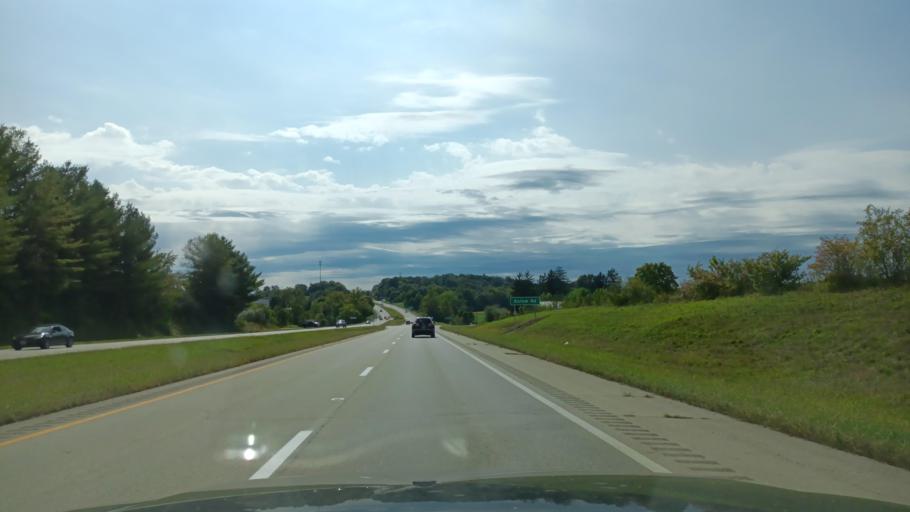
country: US
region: Ohio
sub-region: Athens County
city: Athens
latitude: 39.2543
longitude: -82.1735
